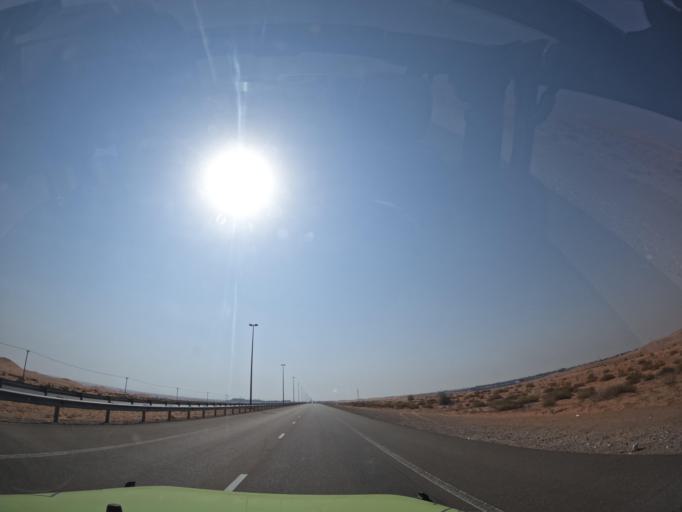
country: OM
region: Al Buraimi
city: Al Buraymi
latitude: 24.4271
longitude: 55.6818
